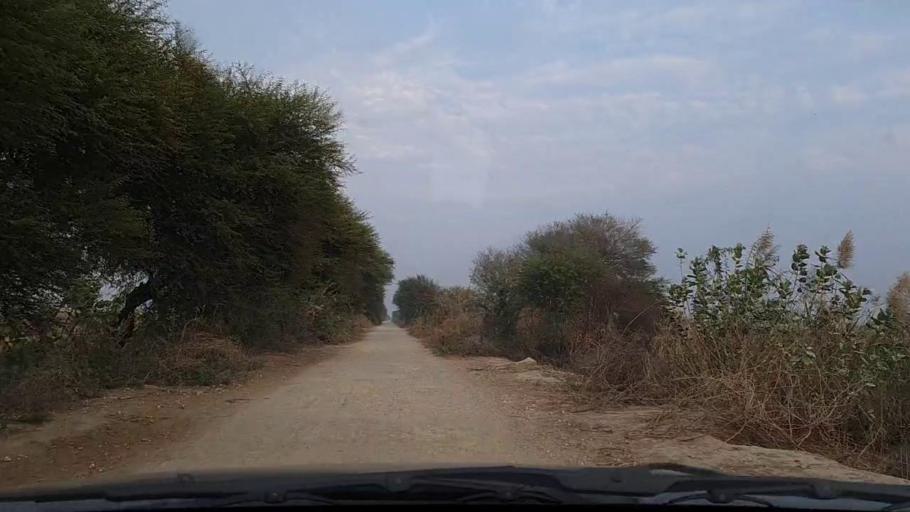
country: PK
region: Sindh
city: Pithoro
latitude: 25.5933
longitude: 69.4765
